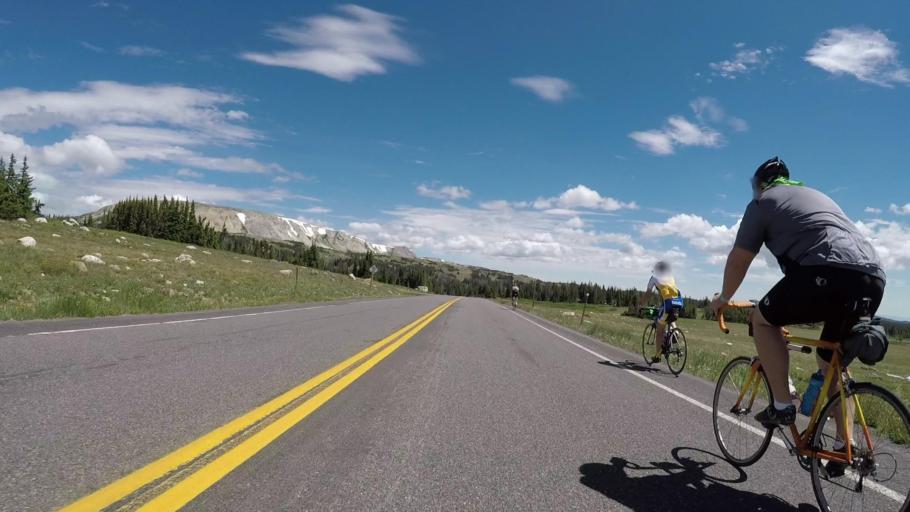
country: US
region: Wyoming
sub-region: Carbon County
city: Saratoga
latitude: 41.3465
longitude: -106.2909
